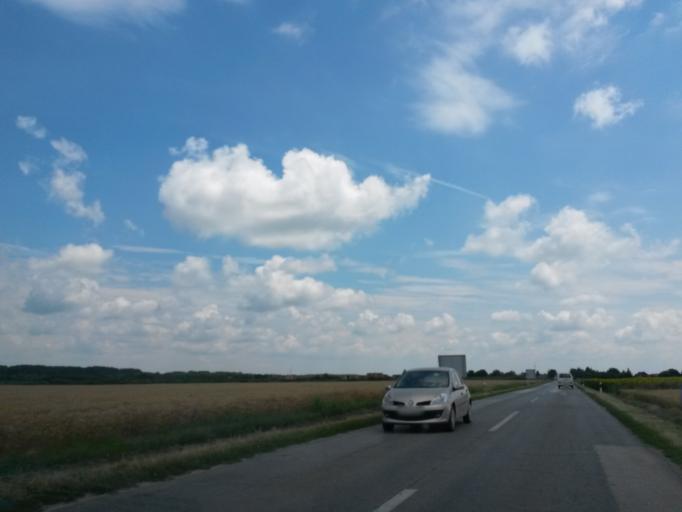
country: HR
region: Osjecko-Baranjska
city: Sarvas
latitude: 45.5320
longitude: 18.8209
